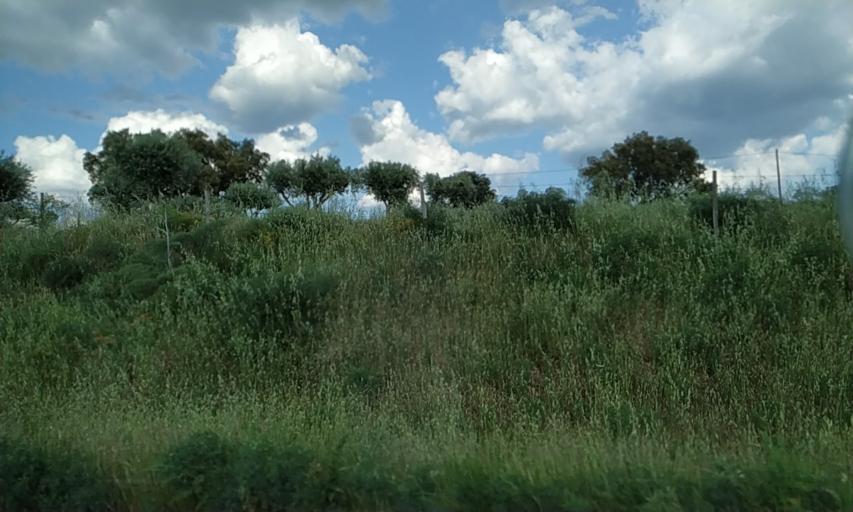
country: PT
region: Portalegre
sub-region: Portalegre
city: Urra
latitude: 39.2375
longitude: -7.4522
